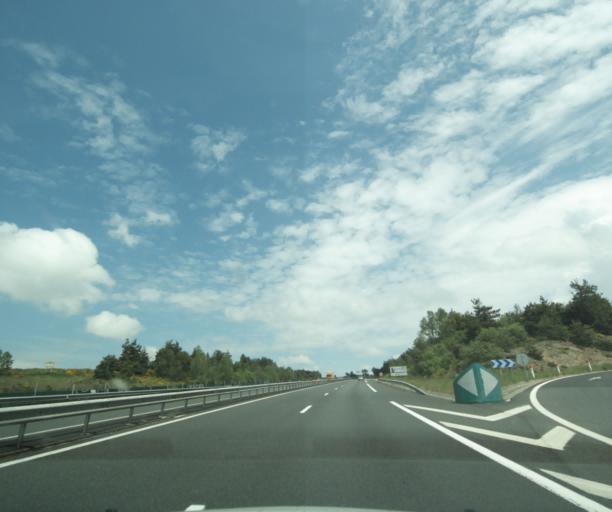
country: FR
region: Auvergne
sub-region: Departement du Cantal
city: Saint-Flour
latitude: 45.0883
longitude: 3.1192
